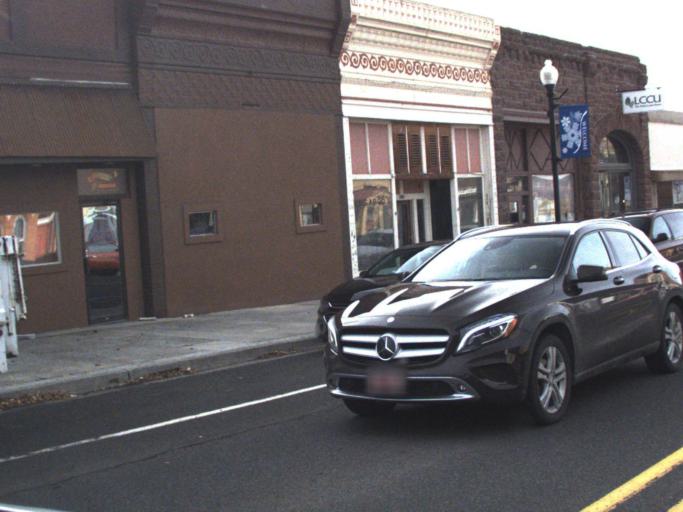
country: US
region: Washington
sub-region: Garfield County
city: Pomeroy
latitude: 46.4744
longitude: -117.5989
